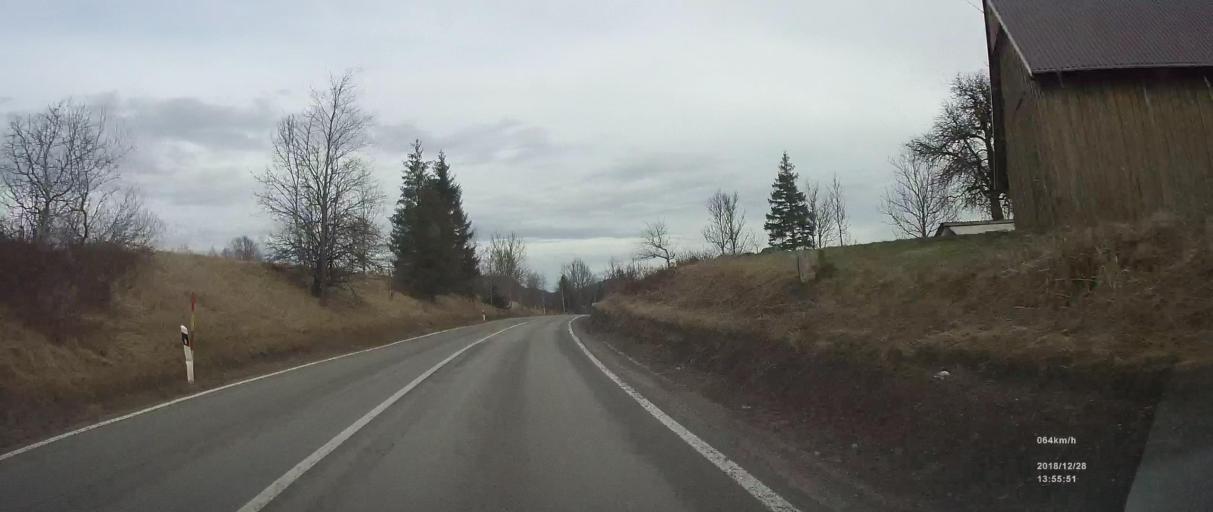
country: HR
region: Primorsko-Goranska
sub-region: Grad Delnice
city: Delnice
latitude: 45.3841
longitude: 14.8811
